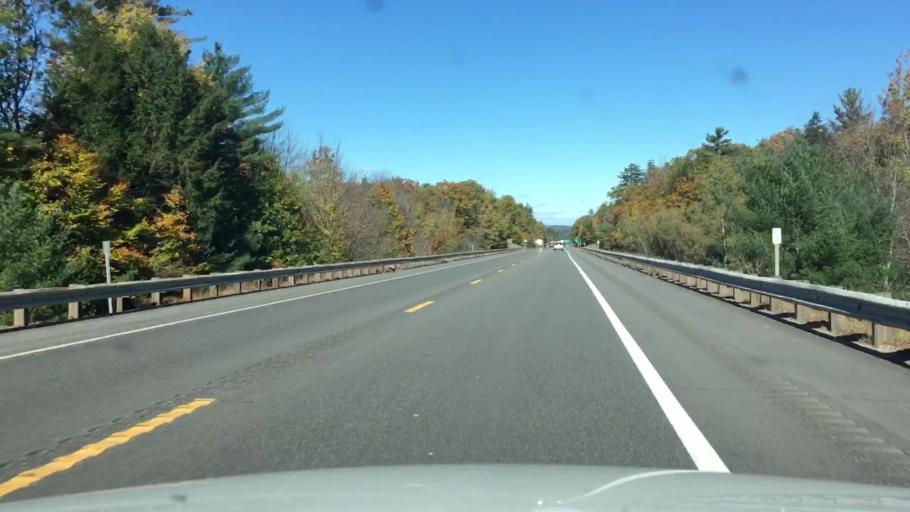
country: US
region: New Hampshire
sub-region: Carroll County
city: Sanbornville
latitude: 43.4647
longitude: -70.9973
